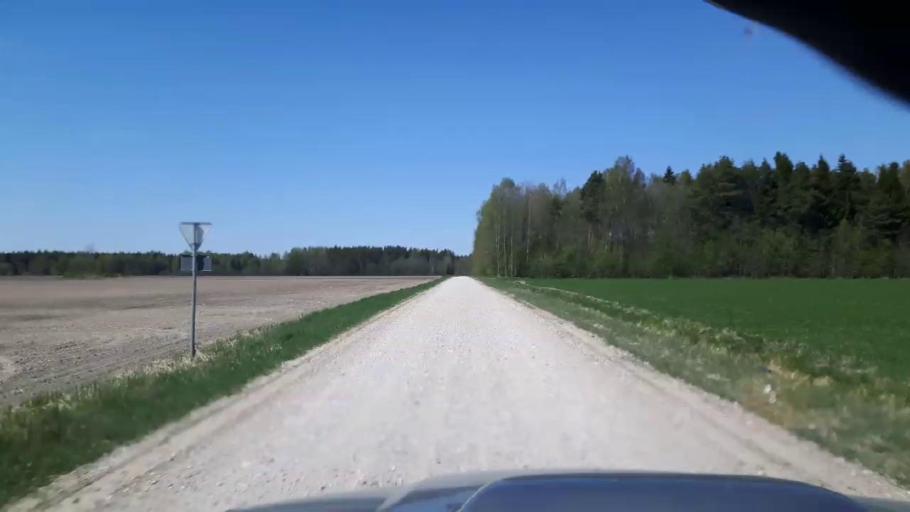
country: EE
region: Paernumaa
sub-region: Tootsi vald
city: Tootsi
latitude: 58.4703
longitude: 24.7701
